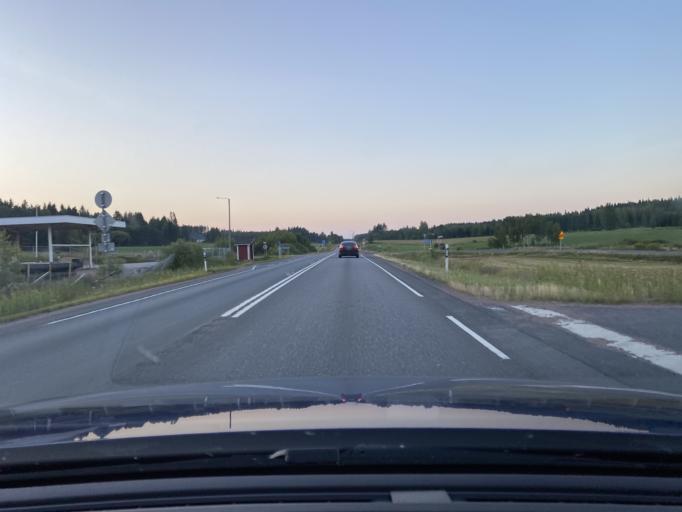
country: FI
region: Pirkanmaa
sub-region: Luoteis-Pirkanmaa
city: Ikaalinen
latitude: 61.8725
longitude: 22.9659
